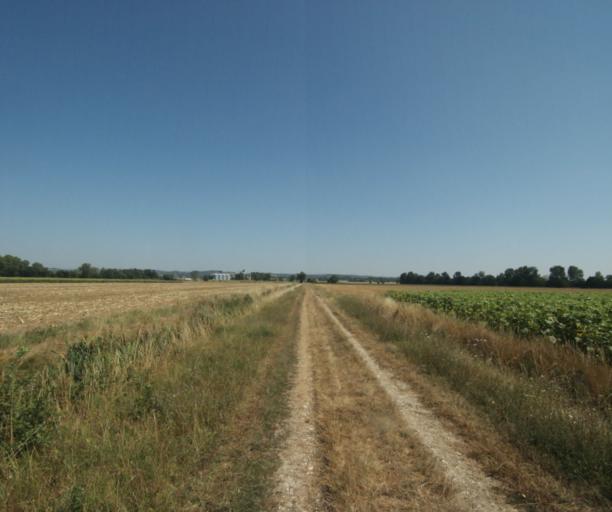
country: FR
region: Midi-Pyrenees
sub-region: Departement de la Haute-Garonne
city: Revel
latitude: 43.5130
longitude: 1.9631
